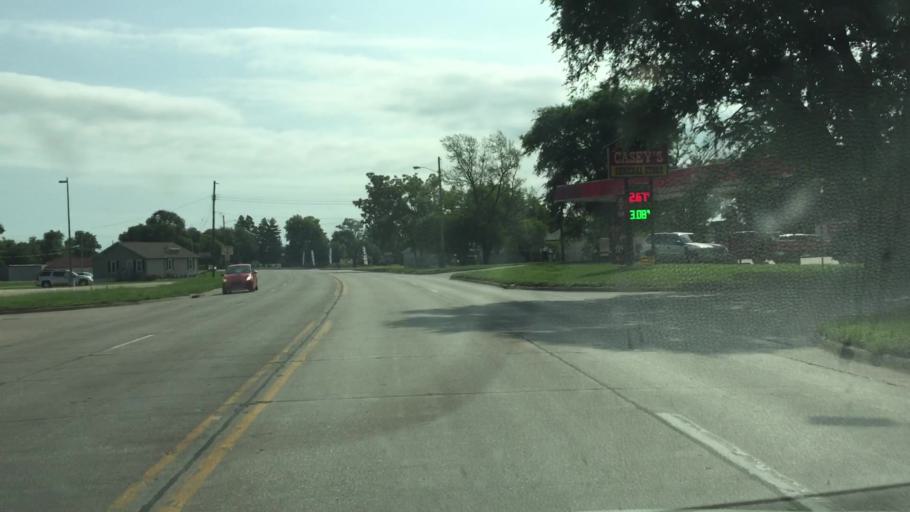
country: US
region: Iowa
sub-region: Lee County
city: Fort Madison
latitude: 40.6242
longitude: -91.3620
